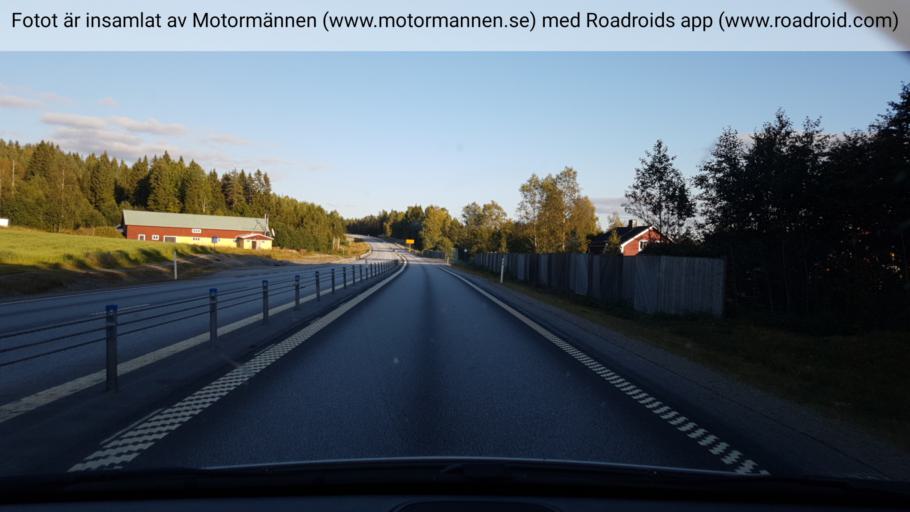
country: SE
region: Vaesterbotten
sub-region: Vannas Kommun
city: Vannasby
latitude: 63.8958
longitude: 19.9210
